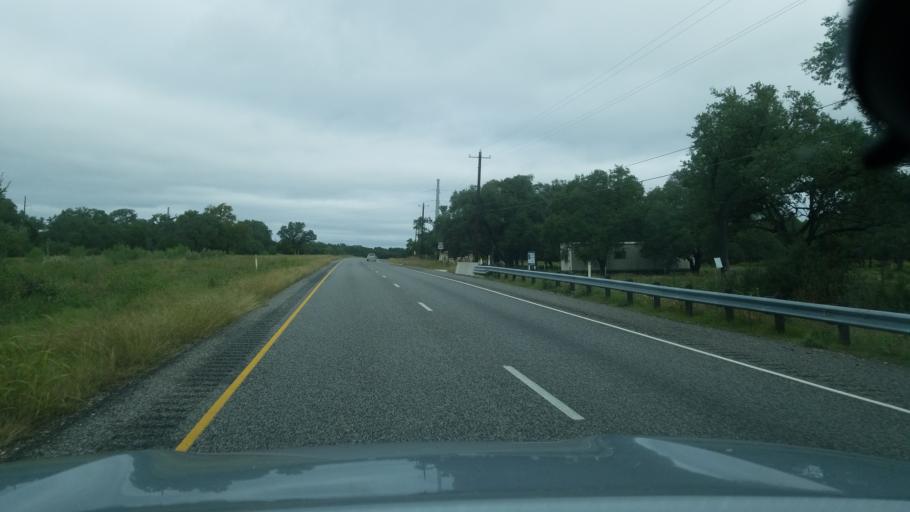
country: US
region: Texas
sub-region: Comal County
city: Canyon Lake
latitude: 29.9107
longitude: -98.4105
